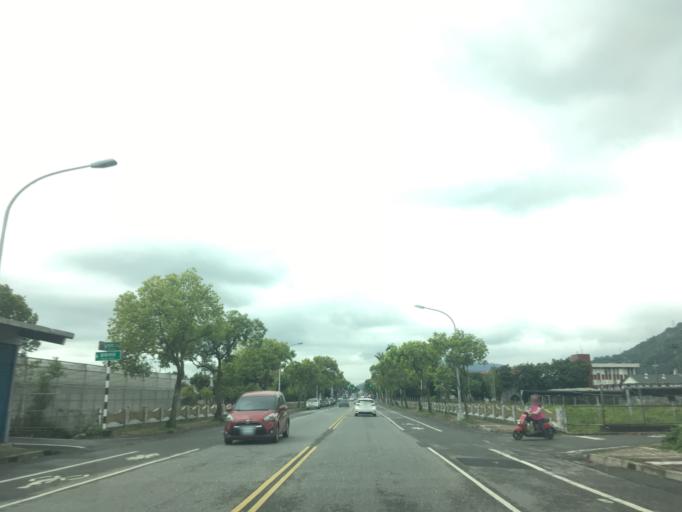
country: TW
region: Taiwan
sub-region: Hualien
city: Hualian
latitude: 23.9766
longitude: 121.5652
